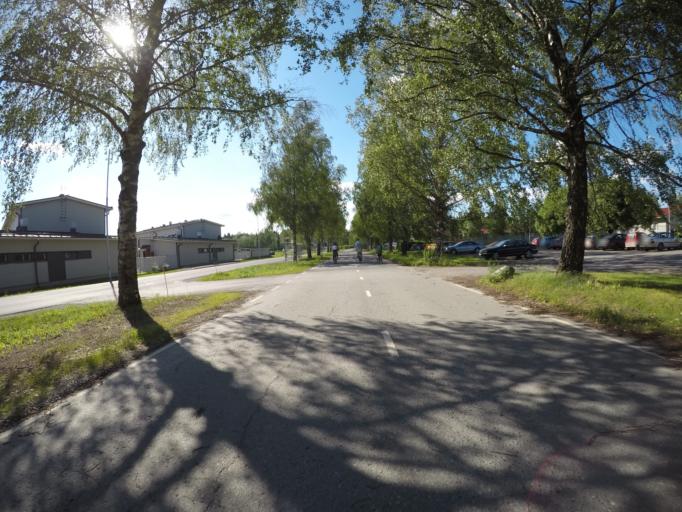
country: FI
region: Haeme
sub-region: Haemeenlinna
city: Haemeenlinna
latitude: 60.9805
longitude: 24.4744
